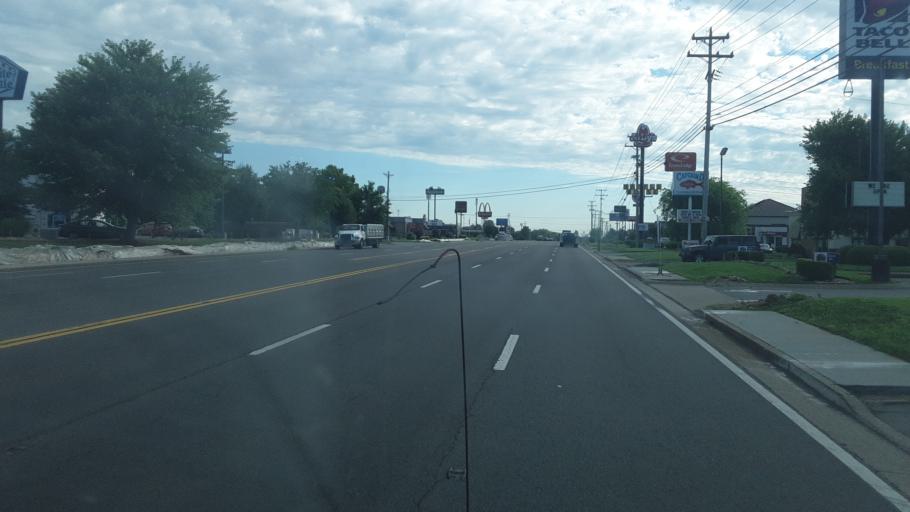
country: US
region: Tennessee
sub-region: Montgomery County
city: Clarksville
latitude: 36.5935
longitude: -87.2890
